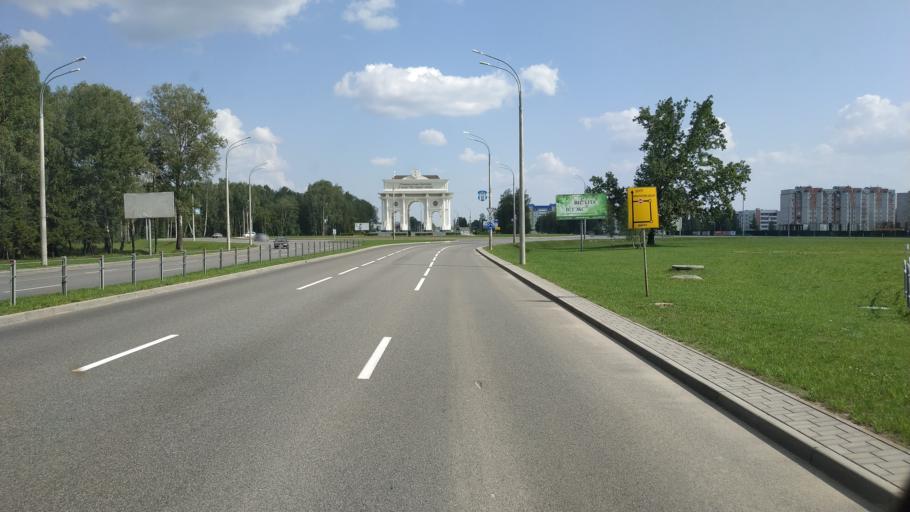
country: BY
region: Mogilev
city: Buynichy
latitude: 53.9375
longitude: 30.2476
